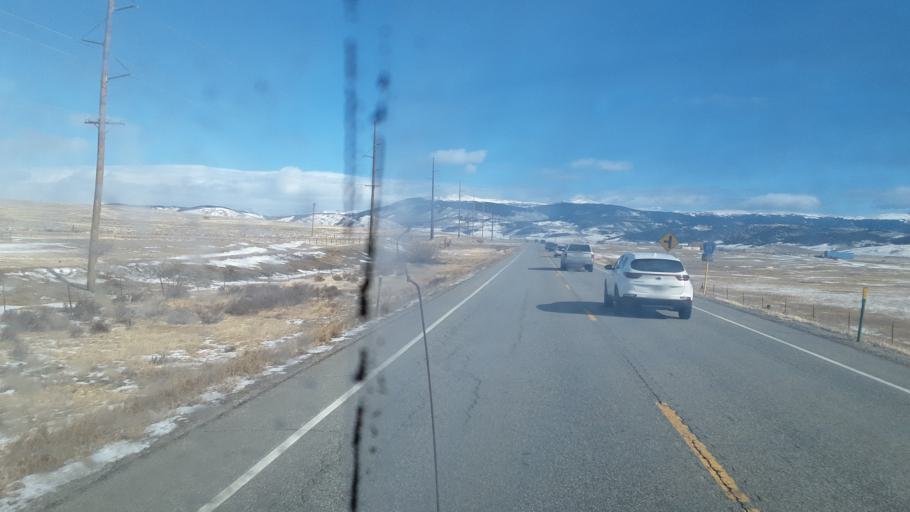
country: US
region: Colorado
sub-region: Park County
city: Fairplay
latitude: 39.3539
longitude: -105.8255
